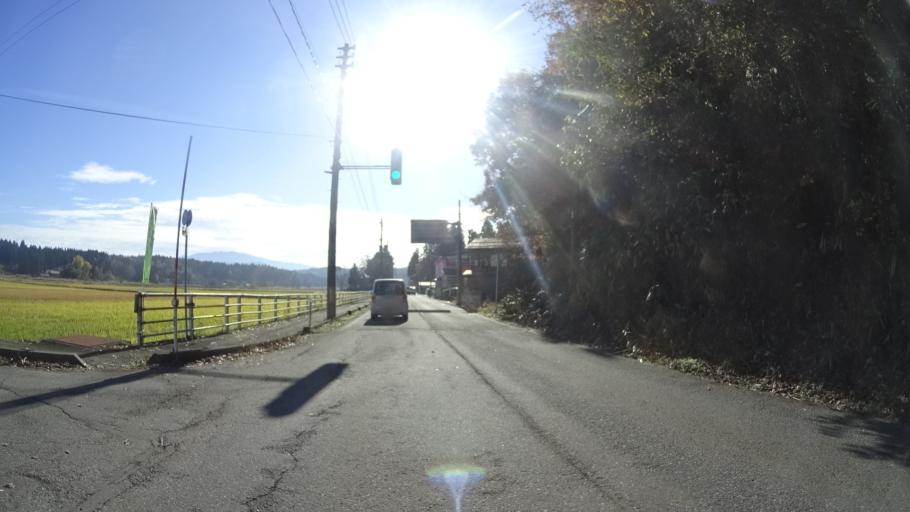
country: JP
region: Niigata
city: Tochio-honcho
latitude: 37.5045
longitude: 138.9711
